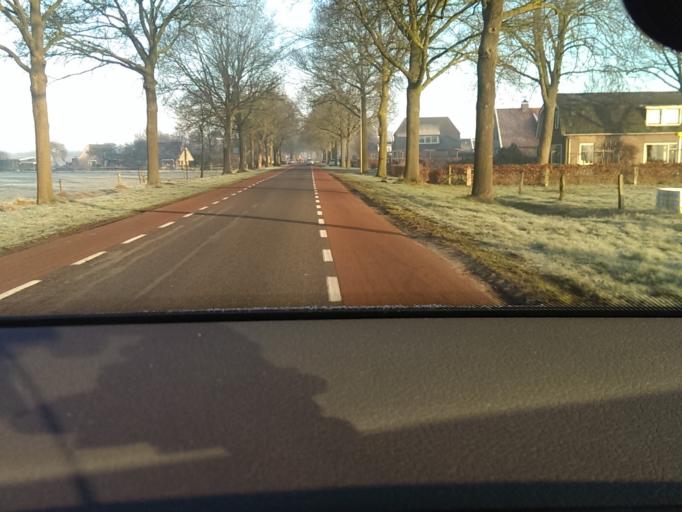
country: NL
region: Overijssel
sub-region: Gemeente Wierden
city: Wierden
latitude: 52.4010
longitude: 6.5755
